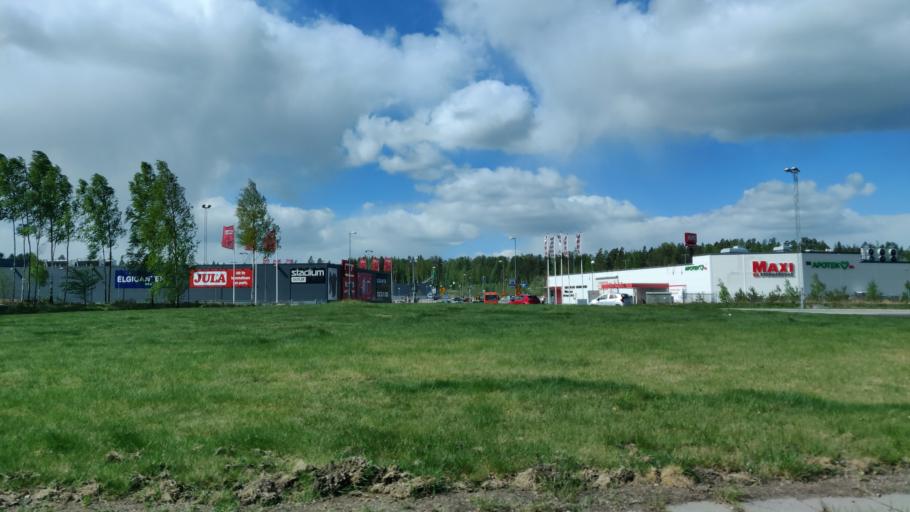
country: SE
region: Vaermland
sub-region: Karlstads Kommun
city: Skattkarr
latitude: 59.3951
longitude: 13.5820
